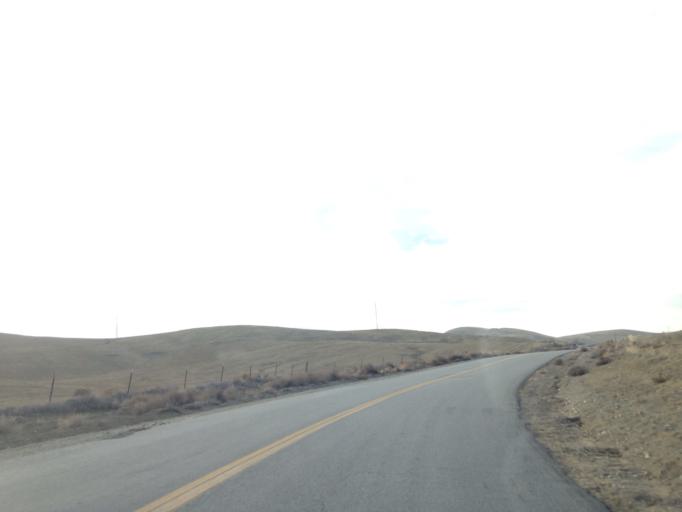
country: US
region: California
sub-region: Kings County
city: Kettleman City
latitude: 35.7266
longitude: -120.0205
